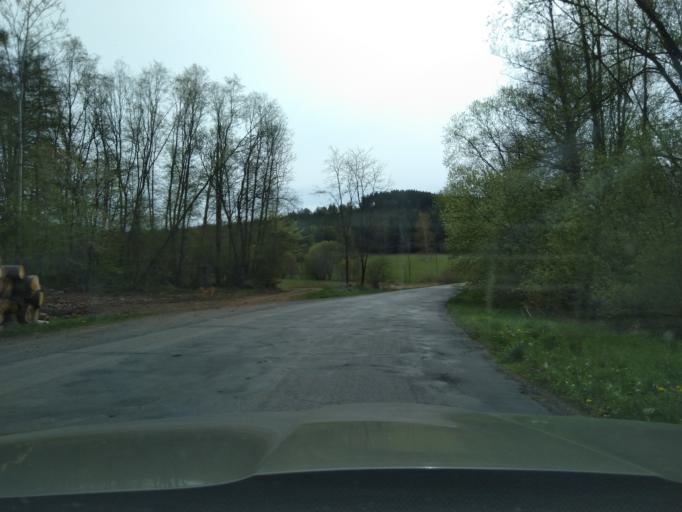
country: CZ
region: Plzensky
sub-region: Okres Klatovy
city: Kasperske Hory
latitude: 49.1932
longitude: 13.6227
